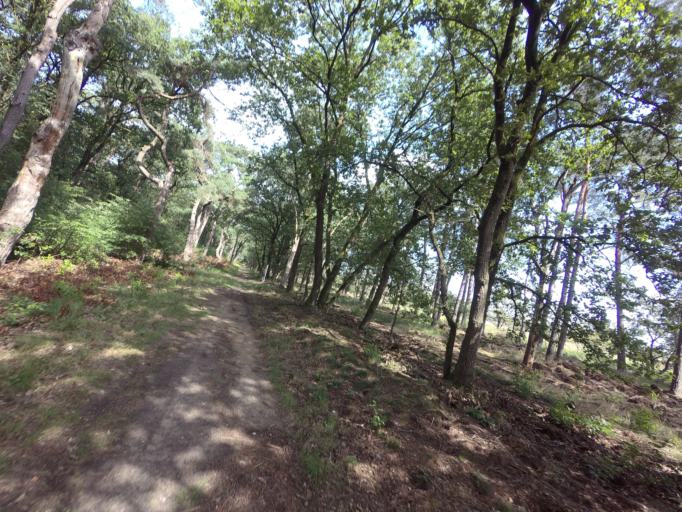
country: NL
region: Gelderland
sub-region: Gemeente Ede
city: Ede
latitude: 52.0565
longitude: 5.6961
